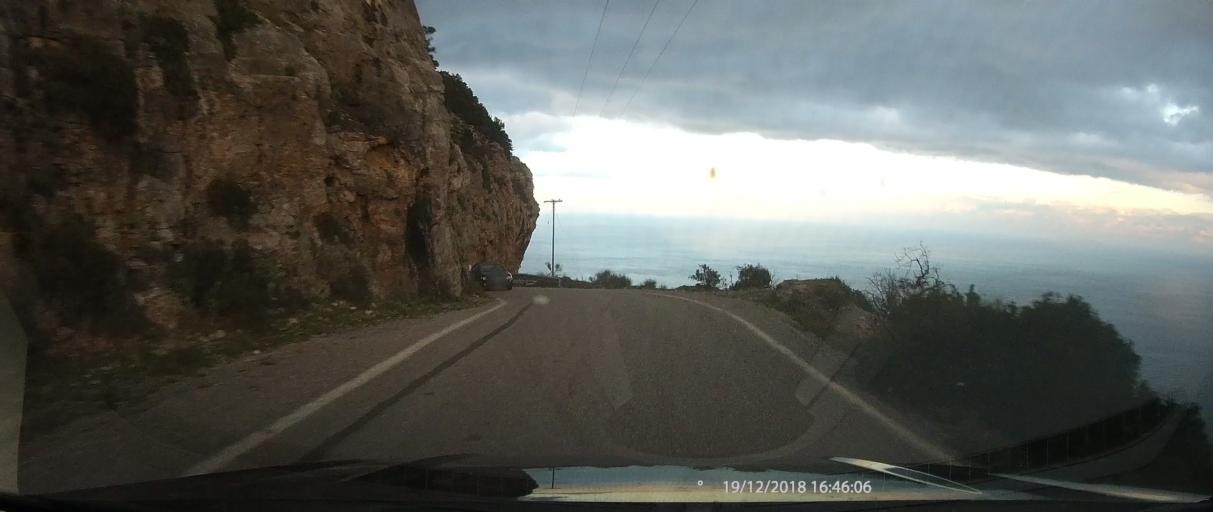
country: GR
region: Peloponnese
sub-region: Nomos Lakonias
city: Sykea
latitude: 36.9216
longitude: 23.0077
